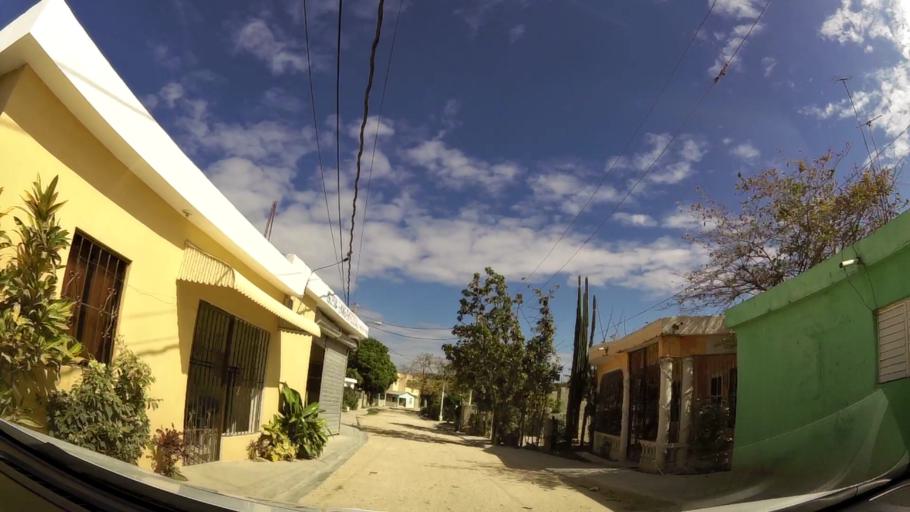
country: DO
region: Santo Domingo
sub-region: Santo Domingo
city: Boca Chica
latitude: 18.4603
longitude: -69.6111
